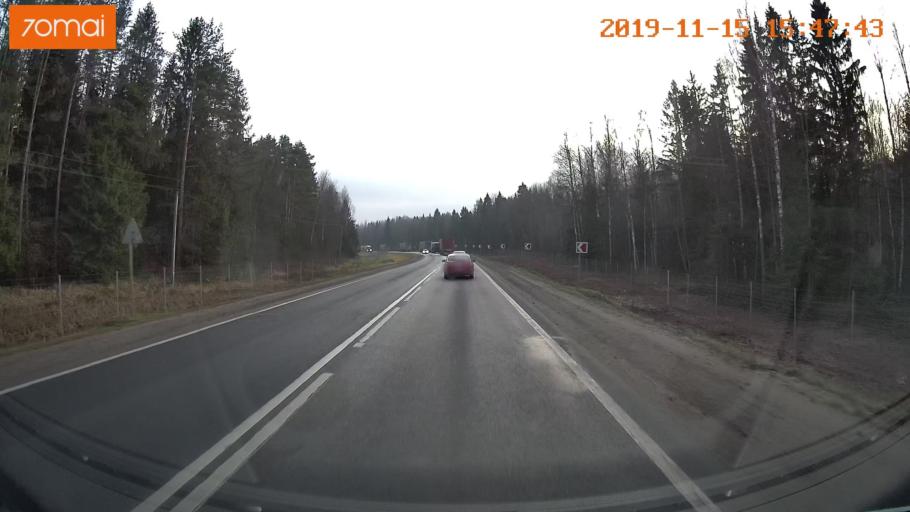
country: RU
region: Jaroslavl
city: Danilov
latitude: 57.9353
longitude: 40.0075
